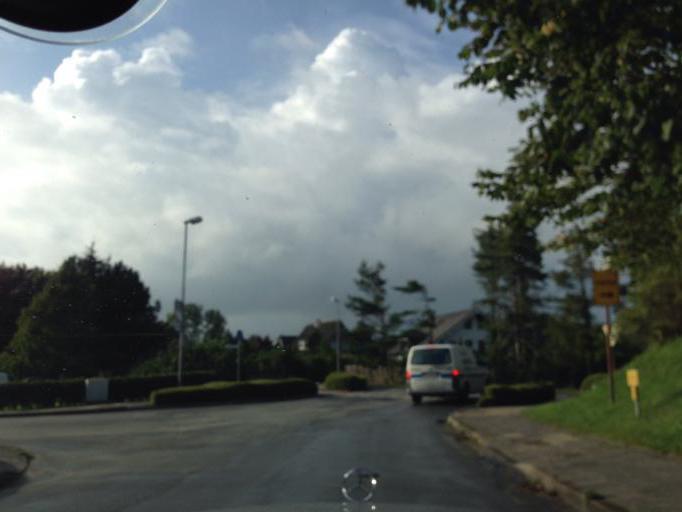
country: DE
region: Schleswig-Holstein
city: Wrixum
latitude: 54.6942
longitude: 8.5568
